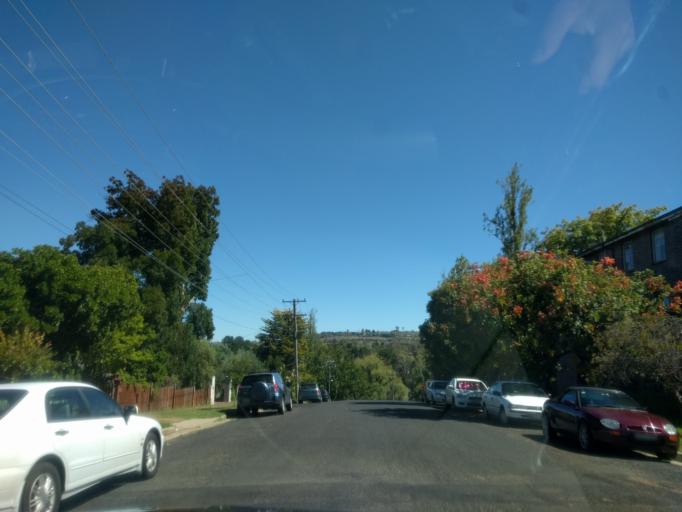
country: AU
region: New South Wales
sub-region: Armidale Dumaresq
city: Armidale
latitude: -30.5236
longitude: 151.6635
